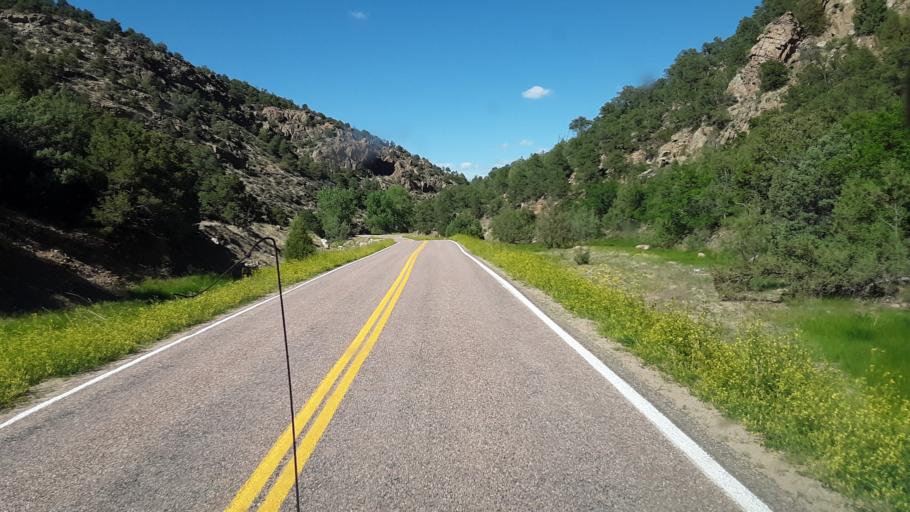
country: US
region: Colorado
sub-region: Fremont County
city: Canon City
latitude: 38.4183
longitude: -105.4118
